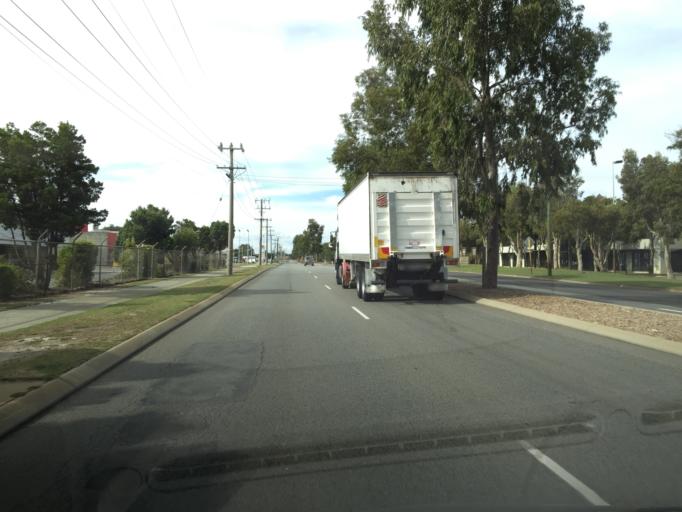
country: AU
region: Western Australia
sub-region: Canning
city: Willetton
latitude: -32.0666
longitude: 115.8993
